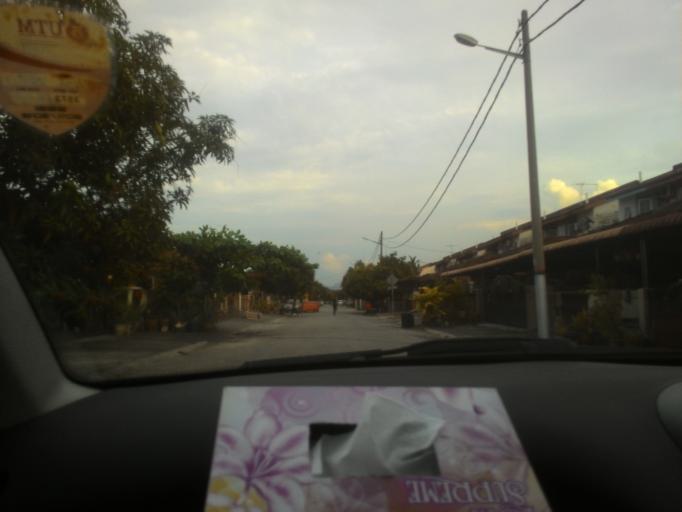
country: MY
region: Perak
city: Ipoh
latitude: 4.6785
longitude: 101.0805
